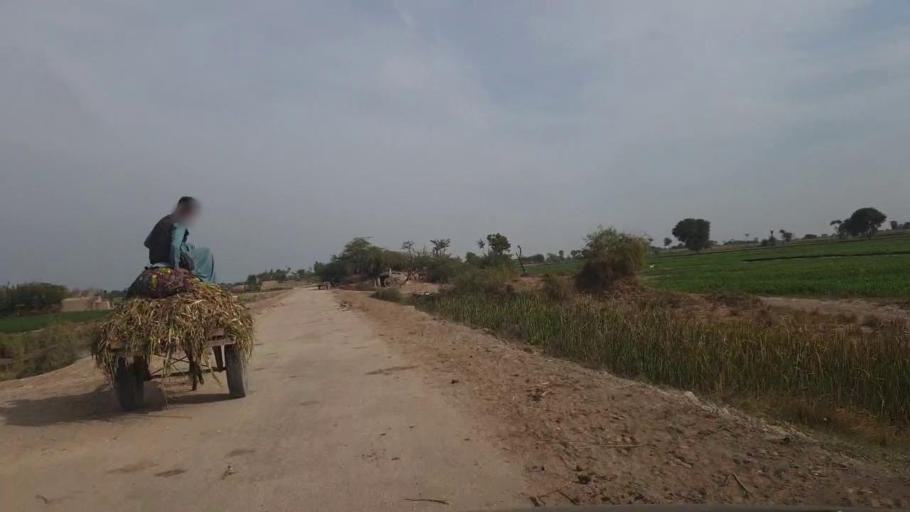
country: PK
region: Sindh
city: Nawabshah
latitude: 26.0909
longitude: 68.4872
